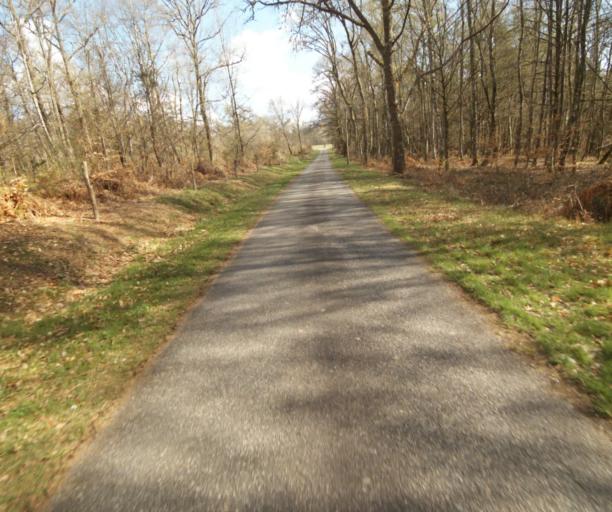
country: FR
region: Limousin
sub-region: Departement de la Correze
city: Laguenne
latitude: 45.2399
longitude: 1.9128
